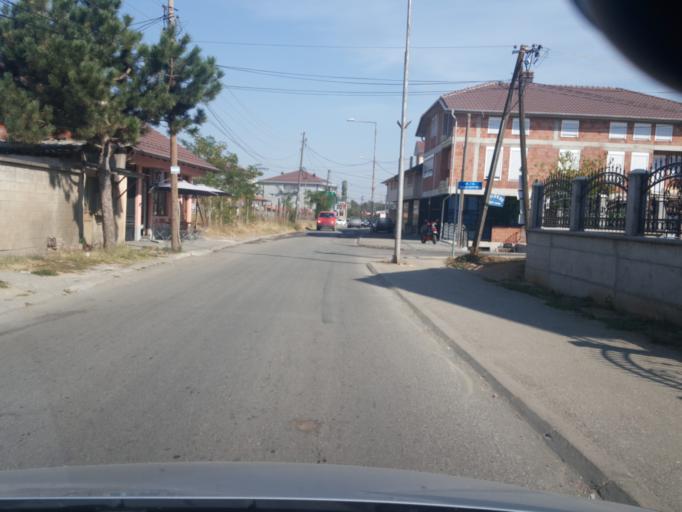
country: XK
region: Gjakova
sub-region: Komuna e Gjakoves
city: Gjakove
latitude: 42.3700
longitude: 20.4151
